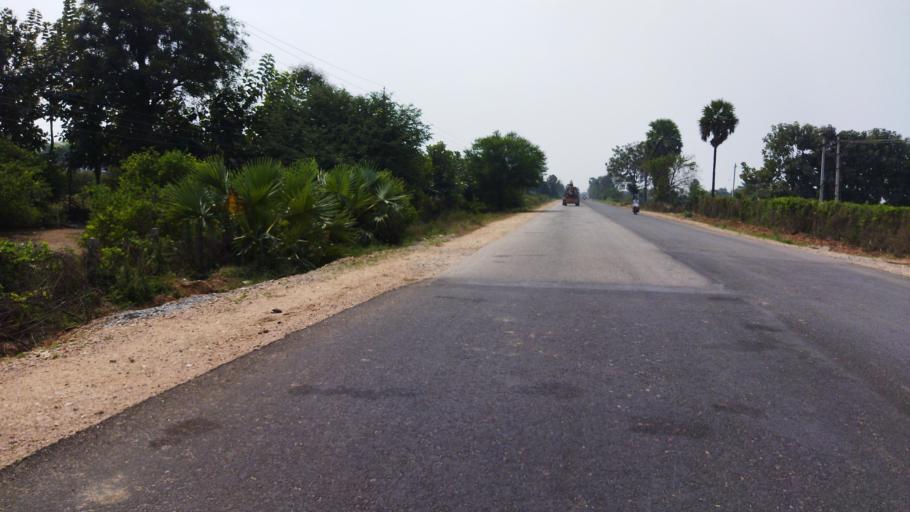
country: IN
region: Telangana
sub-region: Nalgonda
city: Nalgonda
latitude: 17.1002
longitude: 79.3411
